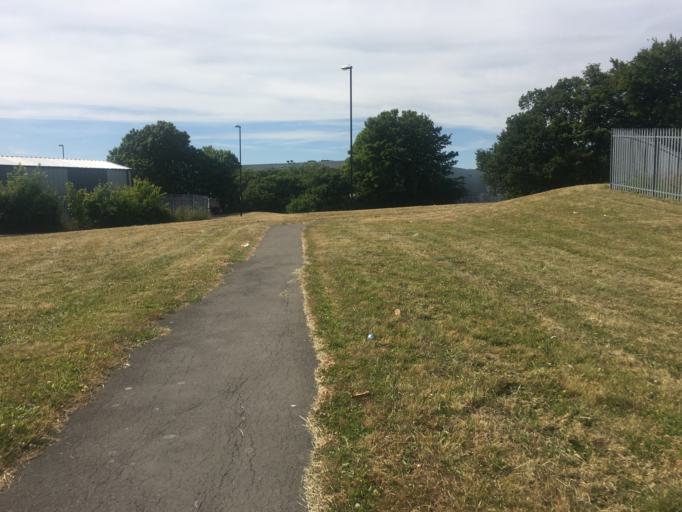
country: GB
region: England
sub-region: Sunderland
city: Washington
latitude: 54.8849
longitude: -1.5384
